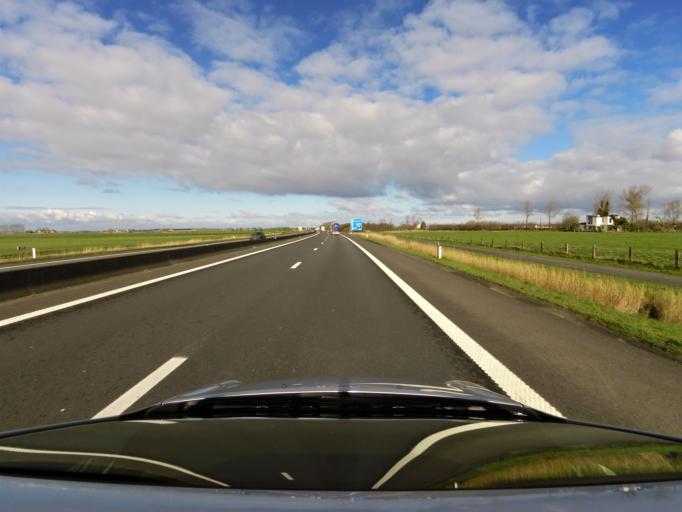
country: BE
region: Flanders
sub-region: Provincie West-Vlaanderen
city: Veurne
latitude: 51.0650
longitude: 2.6350
